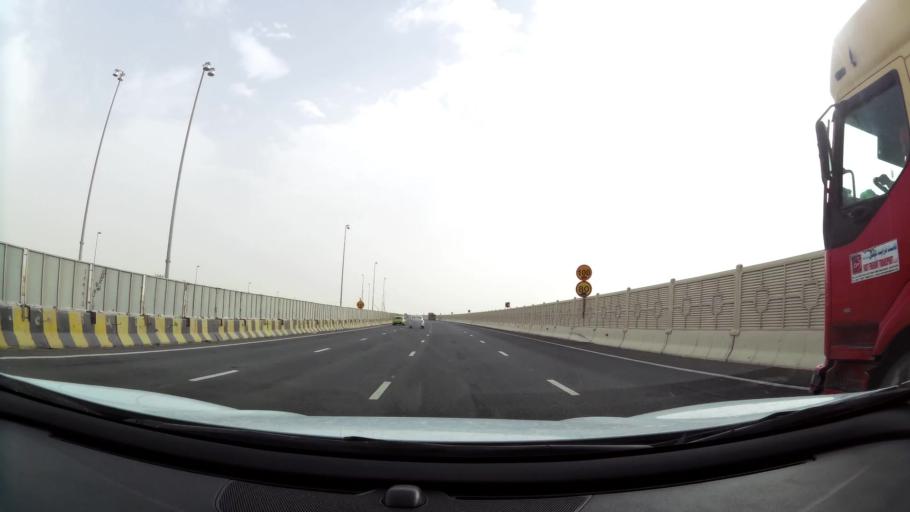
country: AE
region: Abu Dhabi
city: Abu Dhabi
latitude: 24.4496
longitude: 54.6166
